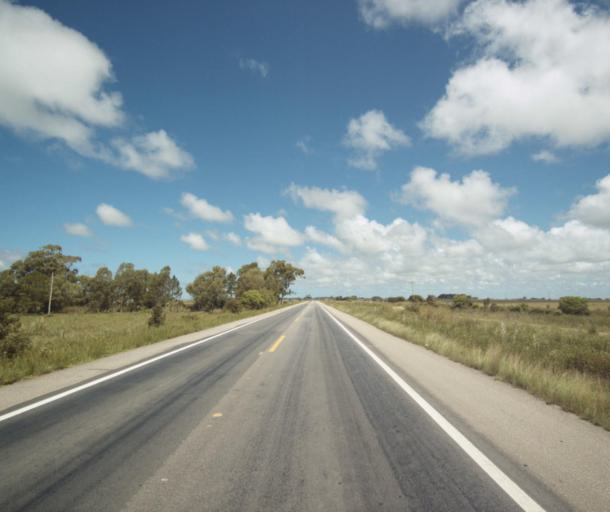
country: BR
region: Rio Grande do Sul
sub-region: Arroio Grande
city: Arroio Grande
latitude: -32.8573
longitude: -52.7058
